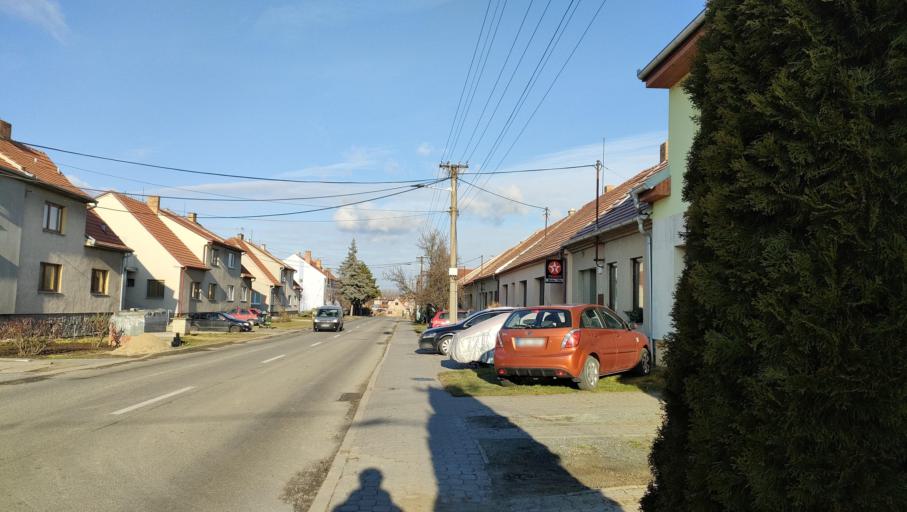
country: CZ
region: South Moravian
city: Sokolnice
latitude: 49.1345
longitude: 16.7329
